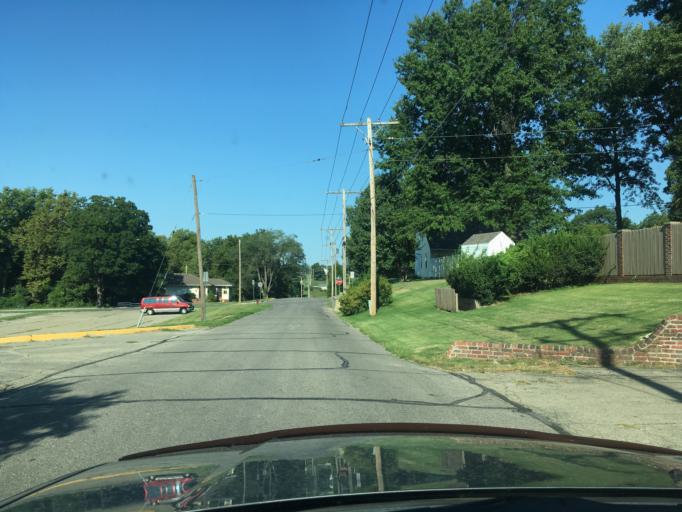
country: US
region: Kansas
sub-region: Atchison County
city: Atchison
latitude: 39.5783
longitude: -95.1155
